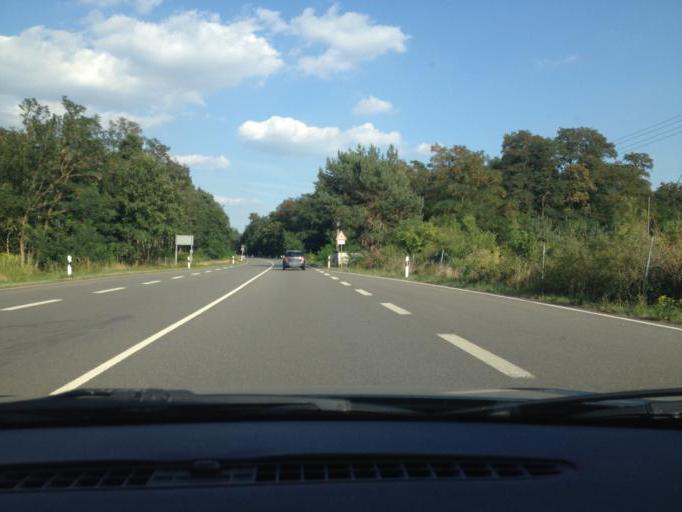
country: DE
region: Rheinland-Pfalz
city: Hanhofen
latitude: 49.3181
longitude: 8.3599
